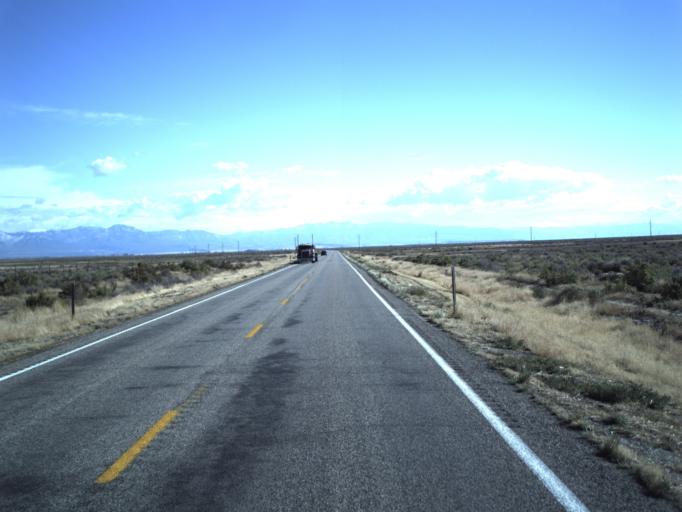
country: US
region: Utah
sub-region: Millard County
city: Delta
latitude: 39.3037
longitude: -112.4733
